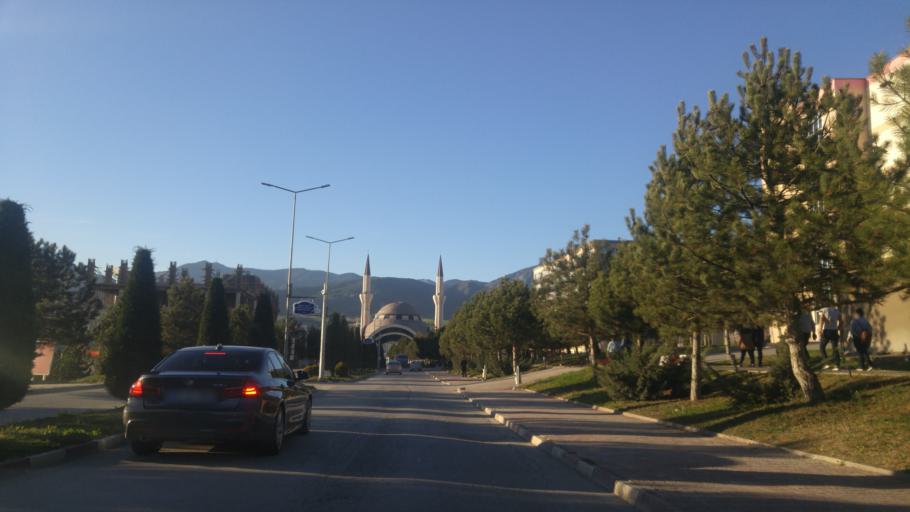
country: TR
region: Karabuk
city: Karabuk
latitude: 41.2097
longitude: 32.6562
